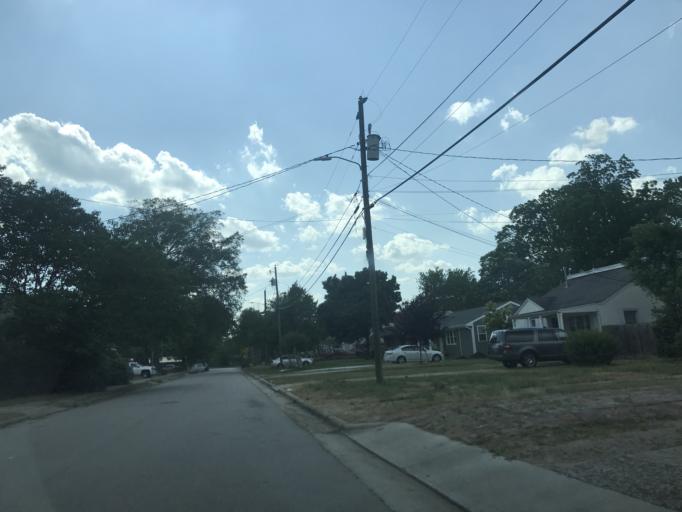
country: US
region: North Carolina
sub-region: Wake County
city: Raleigh
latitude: 35.7789
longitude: -78.6248
